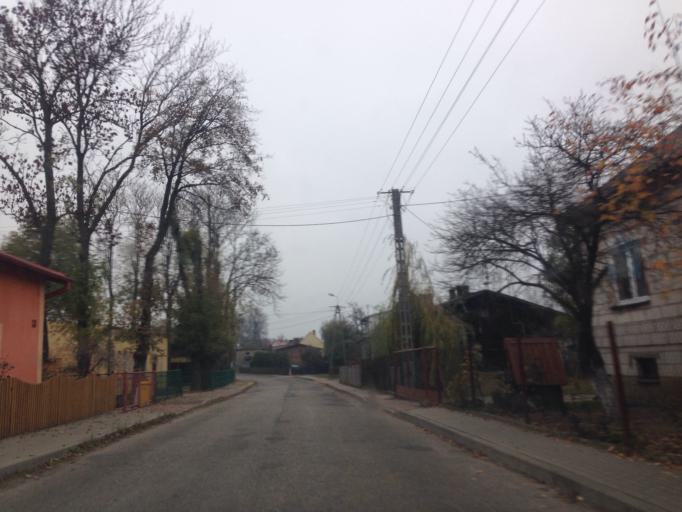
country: PL
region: Kujawsko-Pomorskie
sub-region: Powiat brodnicki
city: Bartniczka
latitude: 53.2266
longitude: 19.5991
